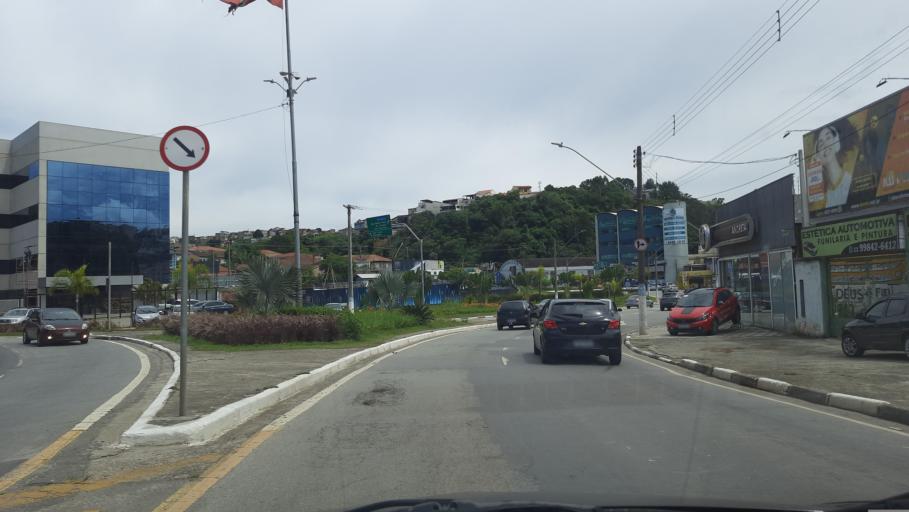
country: BR
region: Sao Paulo
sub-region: Franco Da Rocha
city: Franco da Rocha
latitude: -23.3310
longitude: -46.7287
